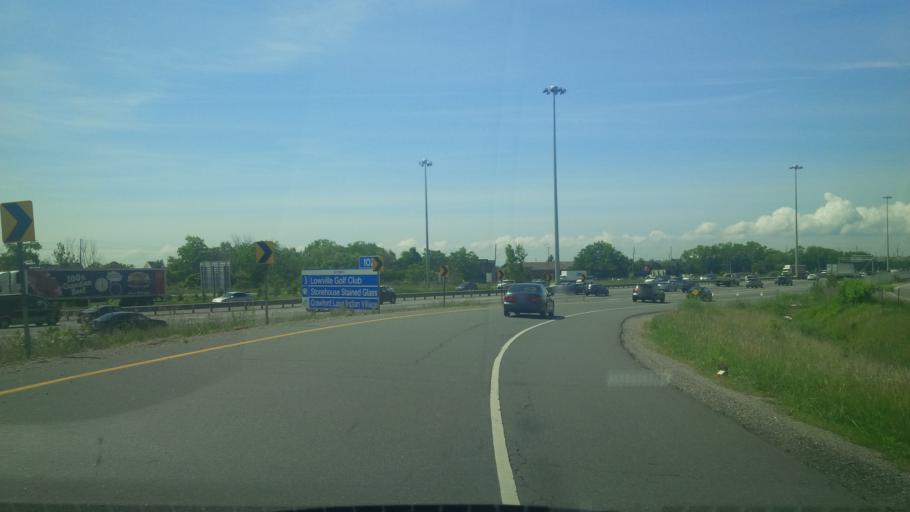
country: CA
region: Ontario
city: Burlington
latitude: 43.3663
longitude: -79.7891
